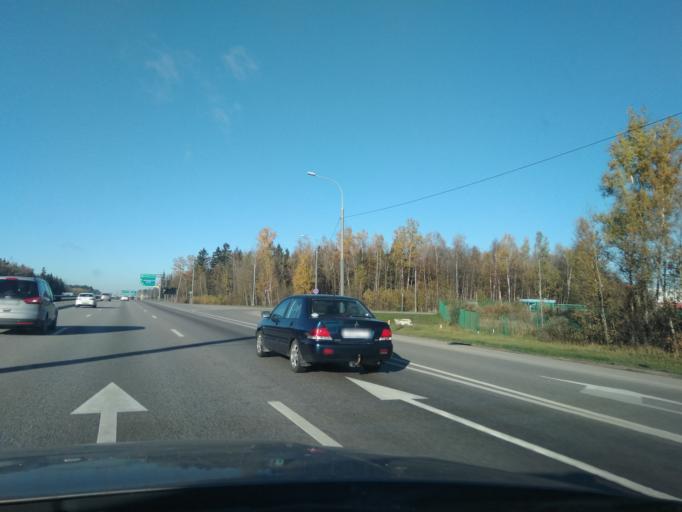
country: RU
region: Moskovskaya
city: Istra
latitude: 55.8496
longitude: 36.8015
